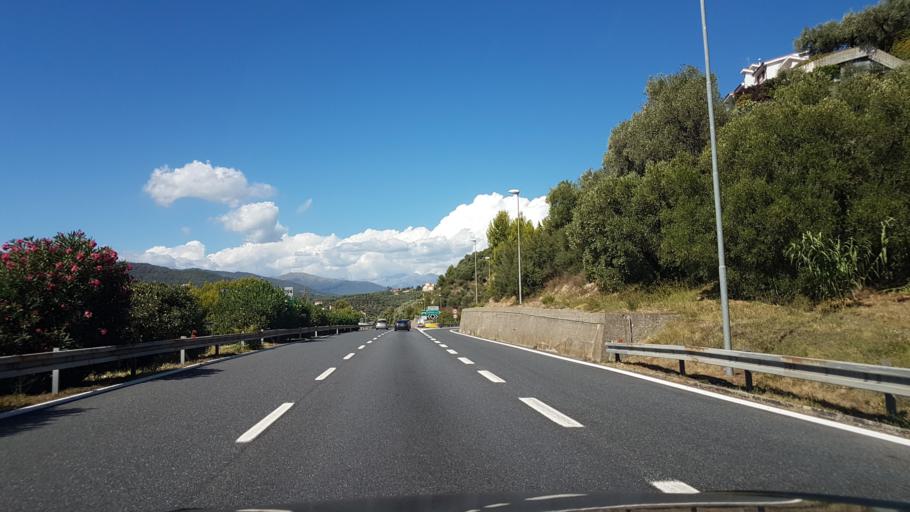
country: IT
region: Liguria
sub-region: Provincia di Imperia
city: Imperia
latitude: 43.9012
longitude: 8.0437
